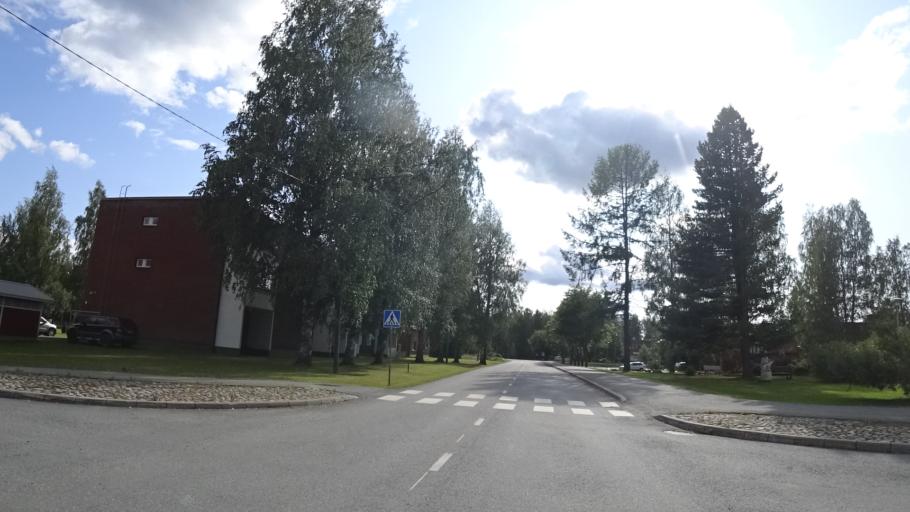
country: FI
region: North Karelia
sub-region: Keski-Karjala
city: Tohmajaervi
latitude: 62.2242
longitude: 30.3337
